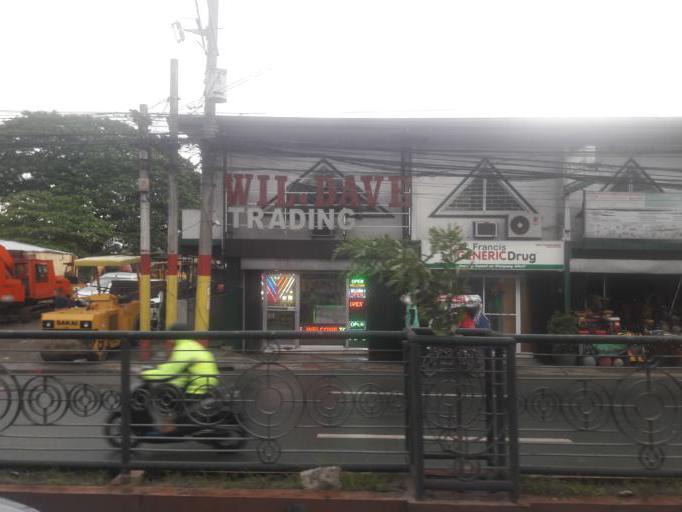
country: PH
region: Calabarzon
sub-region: Province of Cavite
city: Imus
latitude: 14.4302
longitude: 120.9458
